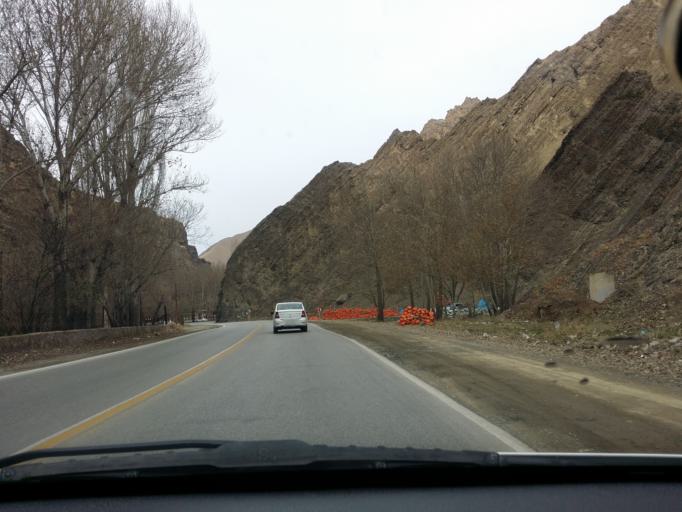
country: IR
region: Tehran
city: Tajrish
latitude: 36.0185
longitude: 51.2698
